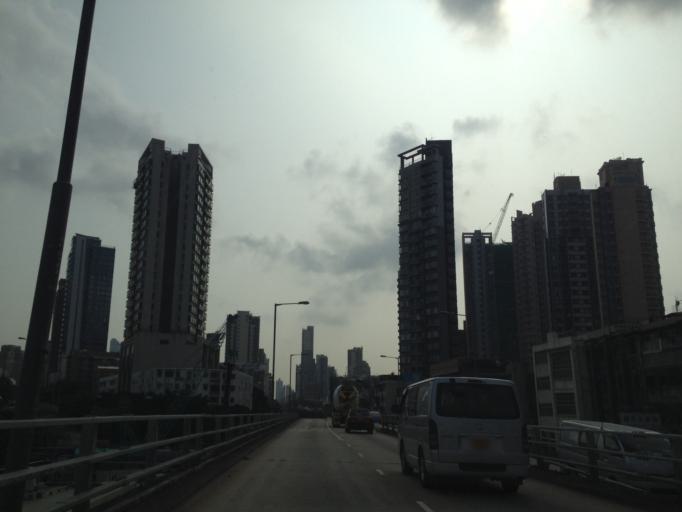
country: HK
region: Kowloon City
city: Kowloon
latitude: 22.3277
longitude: 114.1905
